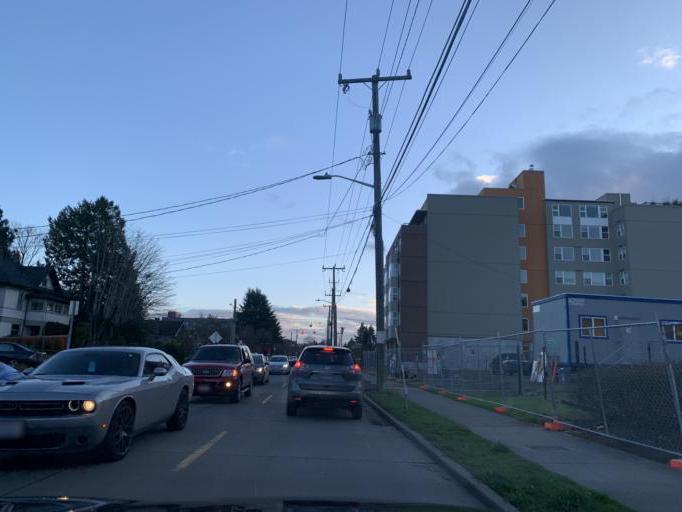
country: US
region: Washington
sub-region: King County
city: Seattle
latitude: 47.5796
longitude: -122.3109
